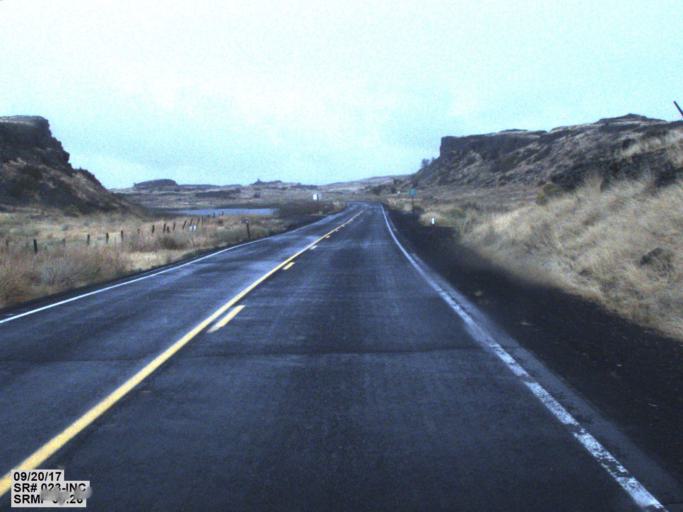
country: US
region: Washington
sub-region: Spokane County
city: Medical Lake
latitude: 47.2586
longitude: -117.9302
